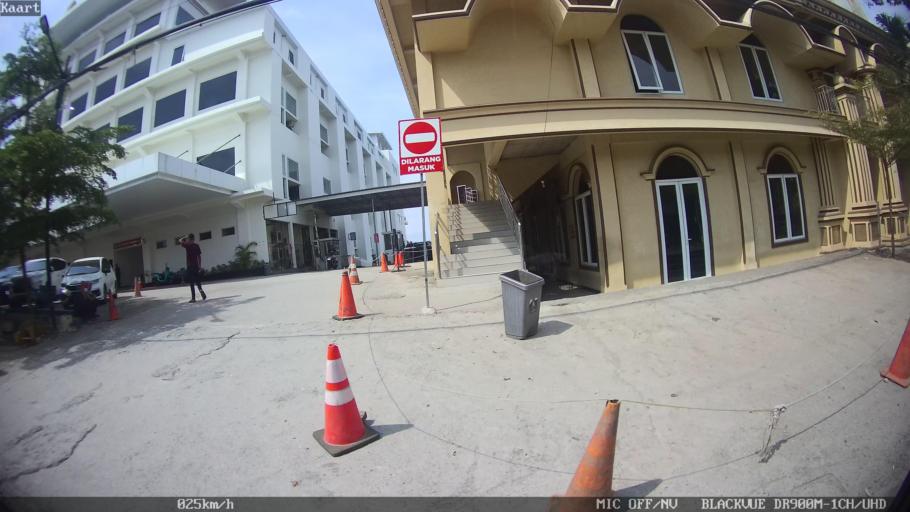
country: ID
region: Lampung
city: Kedaton
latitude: -5.3911
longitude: 105.2767
